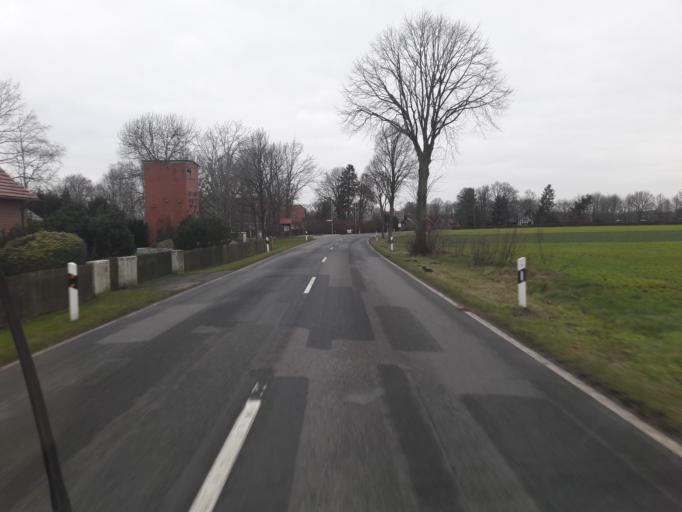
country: DE
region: Lower Saxony
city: Warmsen
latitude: 52.4213
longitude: 8.8563
